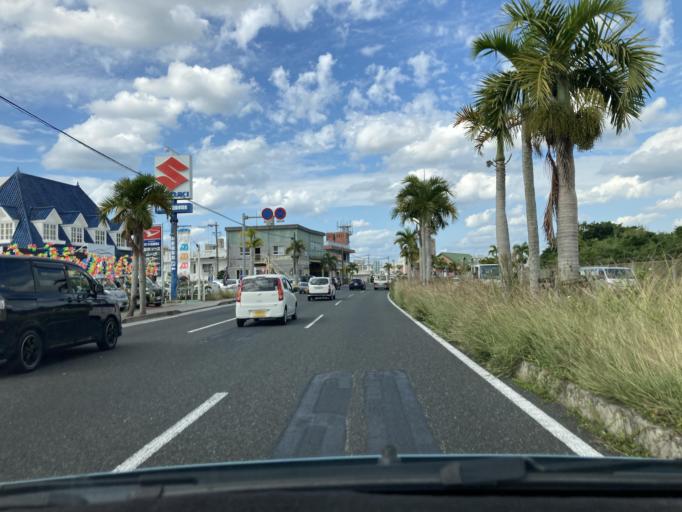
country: JP
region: Okinawa
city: Chatan
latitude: 26.3535
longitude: 127.7457
